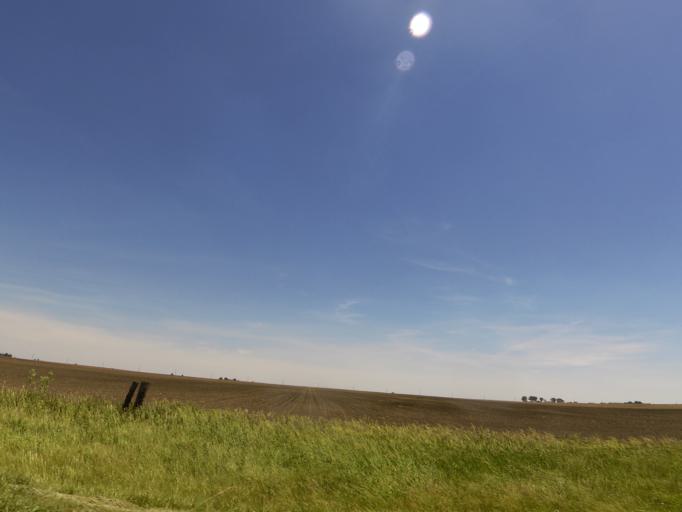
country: US
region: Illinois
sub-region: Vermilion County
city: Hoopeston
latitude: 40.5184
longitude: -87.6917
